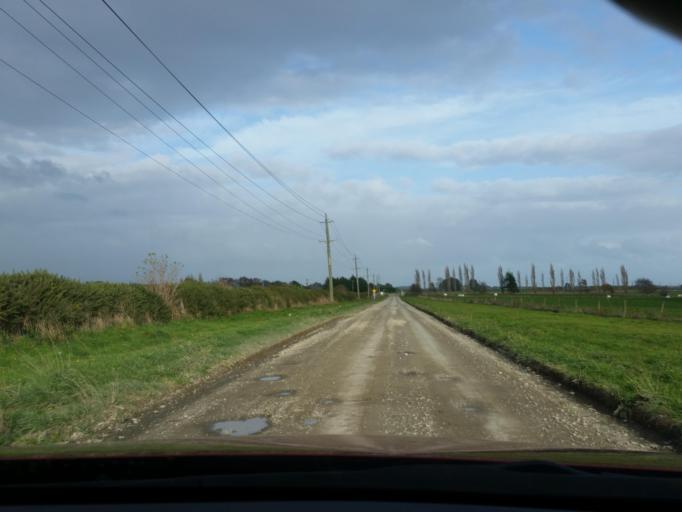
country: NZ
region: Southland
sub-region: Southland District
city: Winton
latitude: -46.2358
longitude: 168.3059
